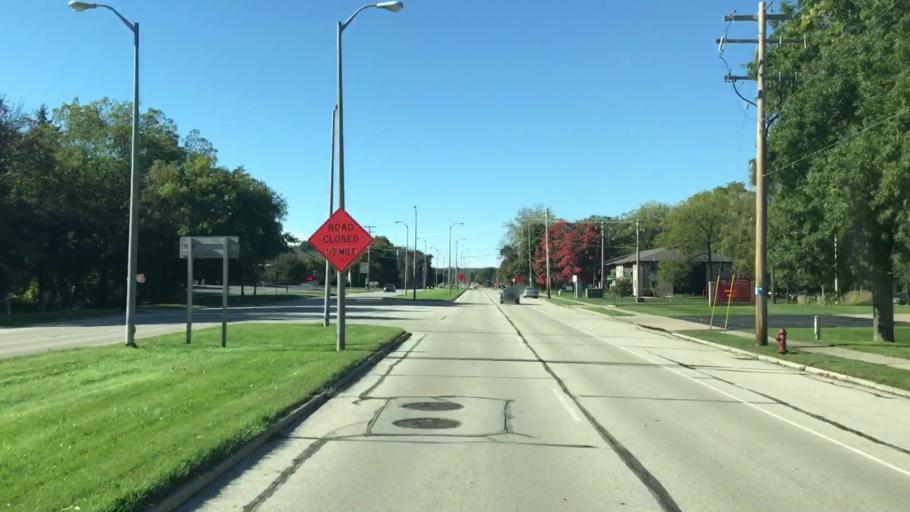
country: US
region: Wisconsin
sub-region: Milwaukee County
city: Hales Corners
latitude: 42.9436
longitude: -88.0380
